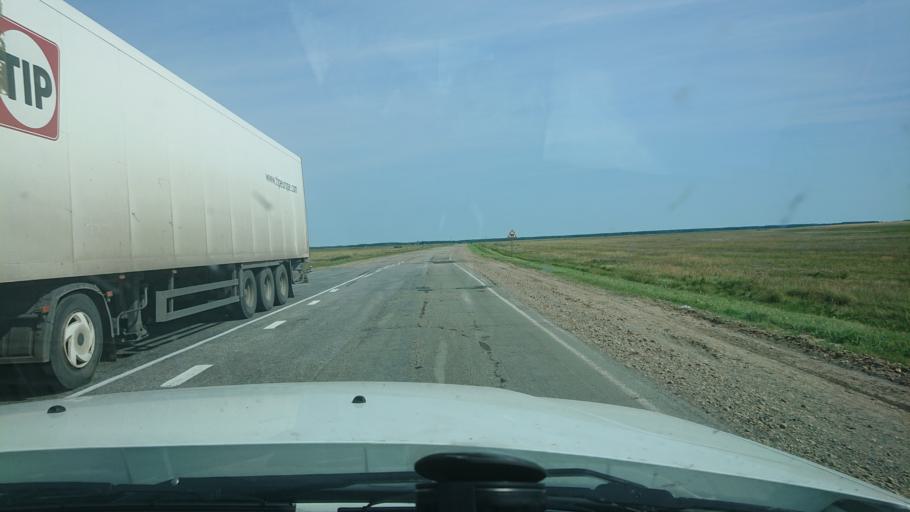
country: RU
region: Tjumen
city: Armizonskoye
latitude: 55.5370
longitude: 67.8973
